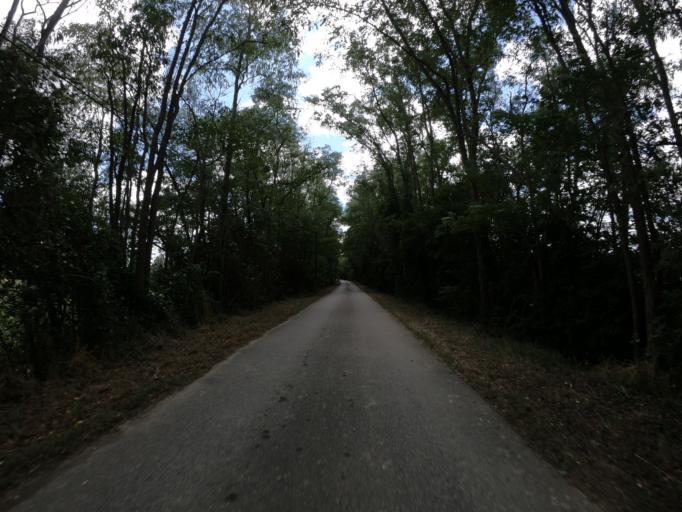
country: FR
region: Midi-Pyrenees
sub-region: Departement de l'Ariege
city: La Tour-du-Crieu
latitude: 43.1016
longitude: 1.7283
